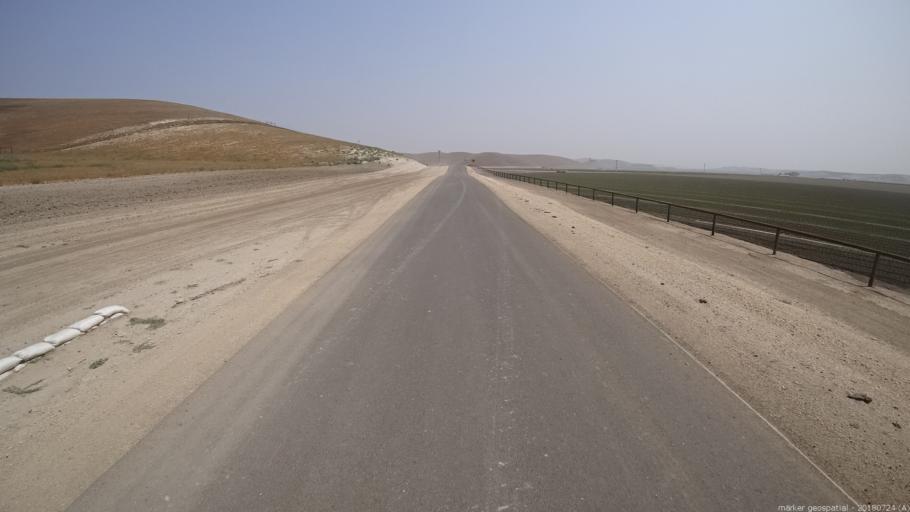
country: US
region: California
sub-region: Monterey County
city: King City
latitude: 36.1894
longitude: -121.0486
